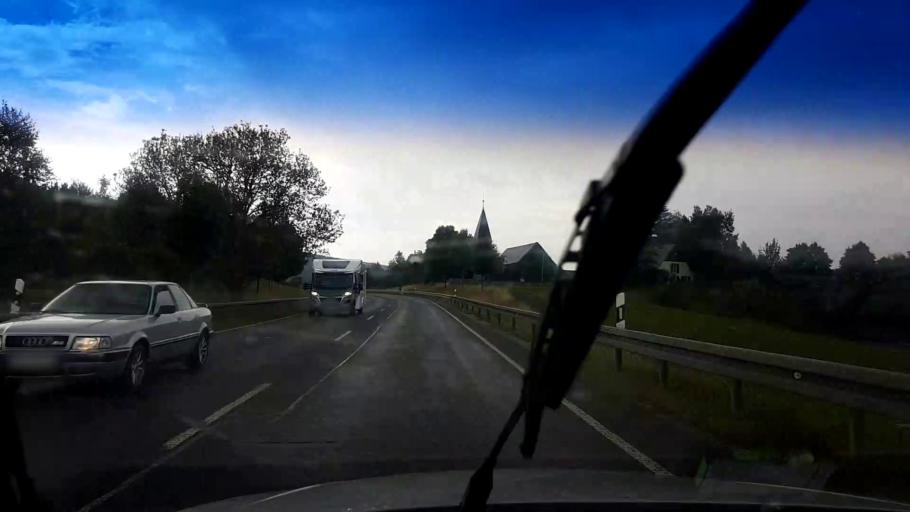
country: DE
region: Bavaria
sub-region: Upper Franconia
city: Trostau
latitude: 50.0157
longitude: 11.9455
